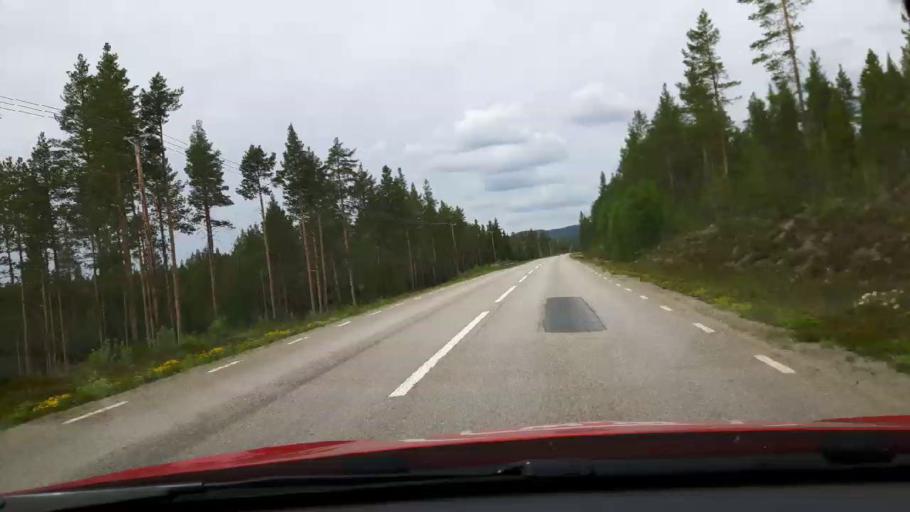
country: SE
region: Jaemtland
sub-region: Harjedalens Kommun
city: Sveg
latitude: 62.3970
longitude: 13.7487
